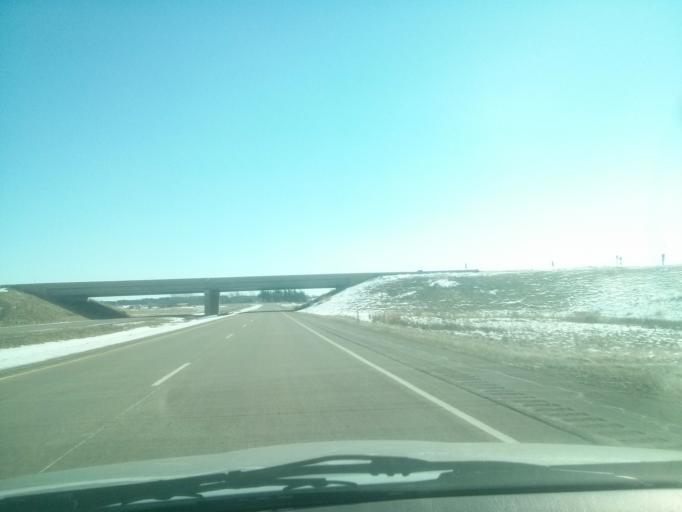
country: US
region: Wisconsin
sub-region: Saint Croix County
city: New Richmond
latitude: 45.1225
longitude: -92.5916
